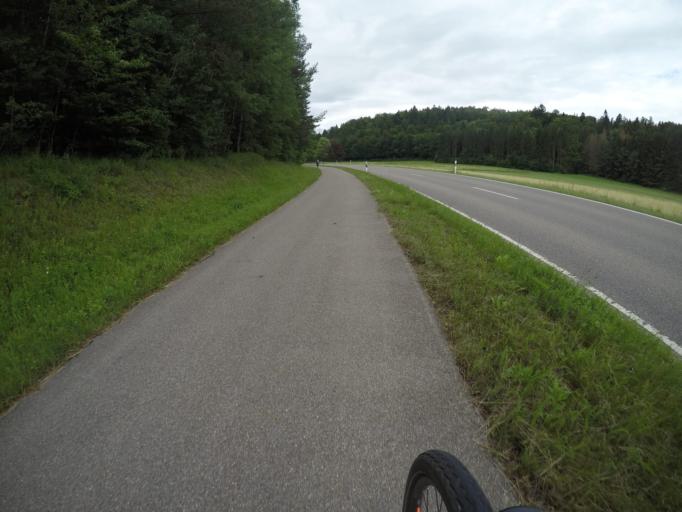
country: DE
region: Baden-Wuerttemberg
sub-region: Regierungsbezirk Stuttgart
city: Aidlingen
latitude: 48.6633
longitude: 8.8762
